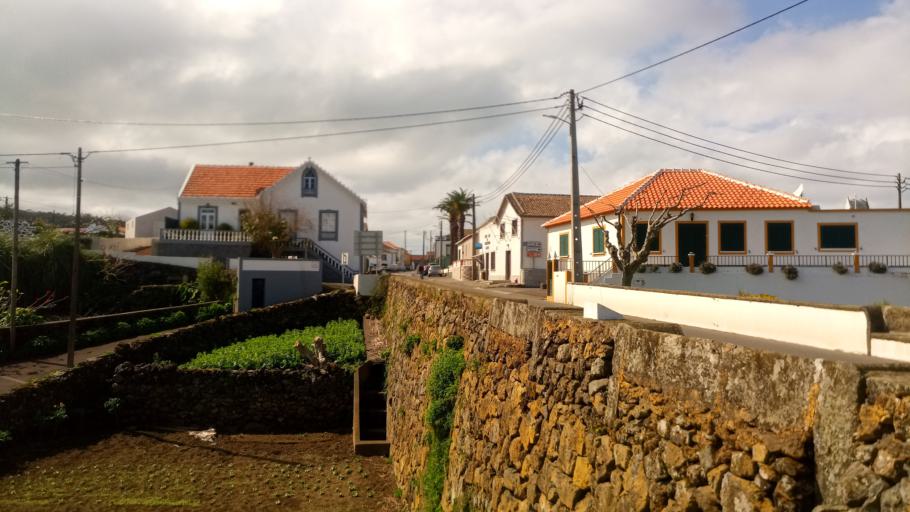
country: PT
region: Azores
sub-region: Praia da Vitoria
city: Biscoitos
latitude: 38.7913
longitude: -27.2996
